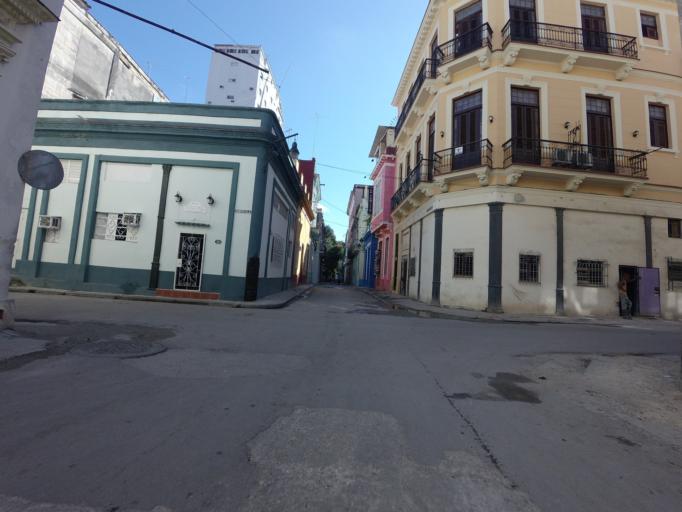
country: CU
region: La Habana
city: Centro Habana
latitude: 23.1394
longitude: -82.3551
